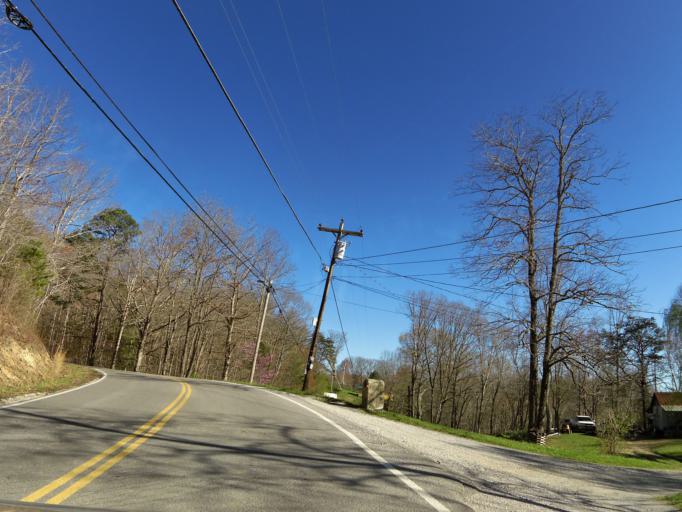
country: US
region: Tennessee
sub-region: Scott County
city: Huntsville
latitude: 36.3560
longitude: -84.3958
